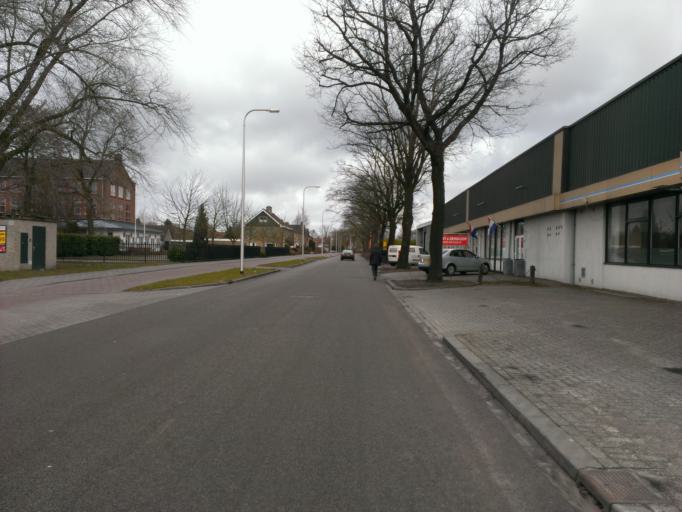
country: NL
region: Drenthe
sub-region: Gemeente Hoogeveen
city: Hoogeveen
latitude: 52.7322
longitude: 6.4777
